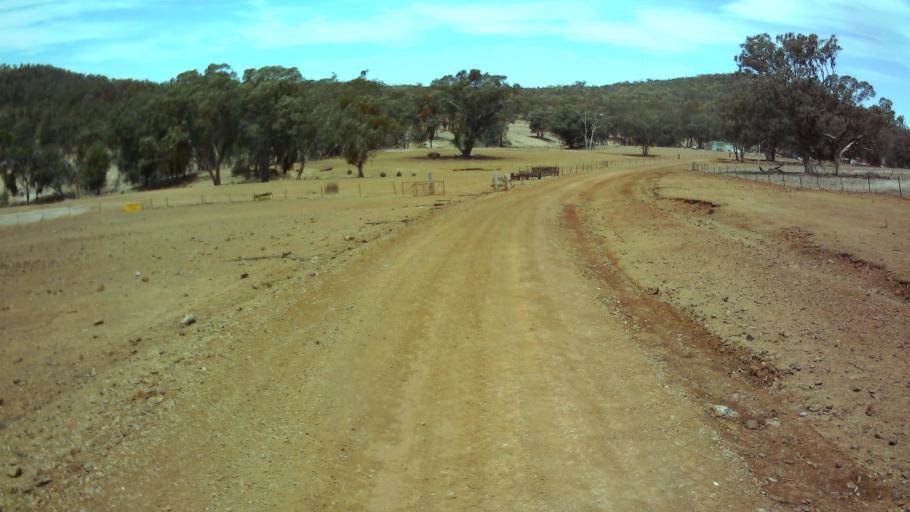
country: AU
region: New South Wales
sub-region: Weddin
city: Grenfell
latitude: -33.7904
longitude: 148.1586
